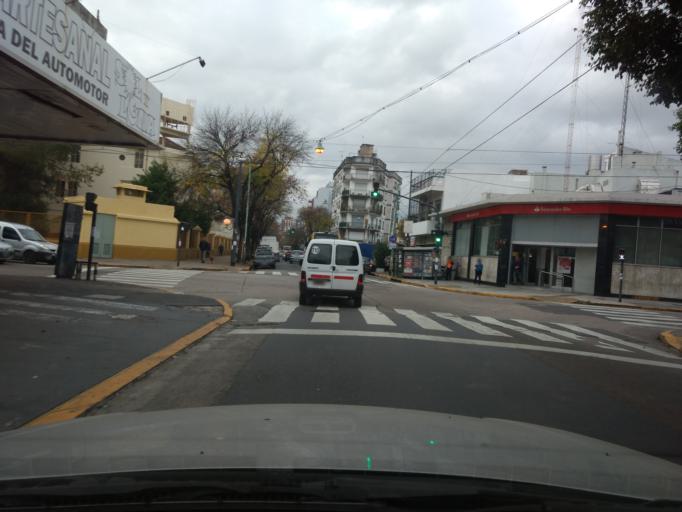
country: AR
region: Buenos Aires F.D.
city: Villa Santa Rita
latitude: -34.6179
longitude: -58.5027
